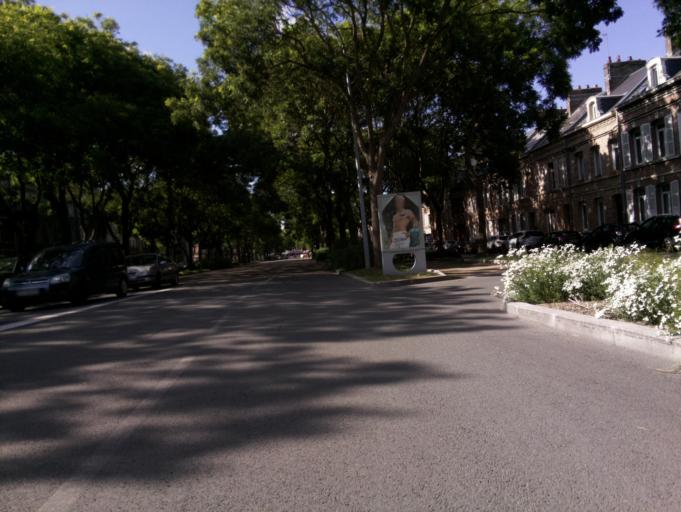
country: FR
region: Picardie
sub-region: Departement de la Somme
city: Amiens
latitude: 49.8944
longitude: 2.2839
